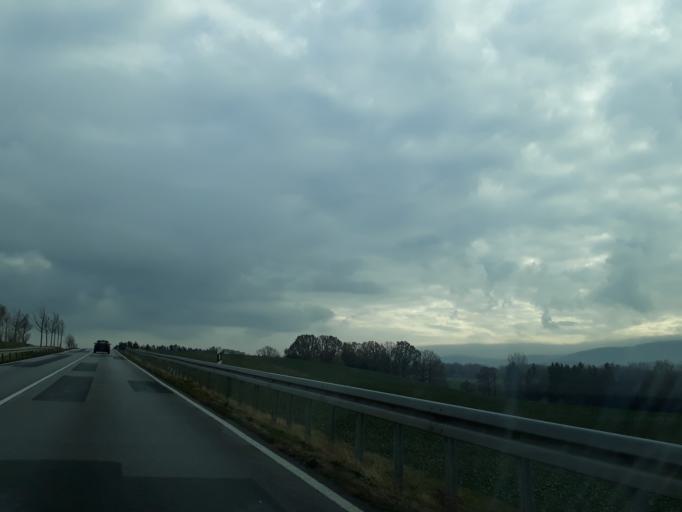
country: DE
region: Saxony
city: Kubschutz
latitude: 51.1681
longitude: 14.4906
